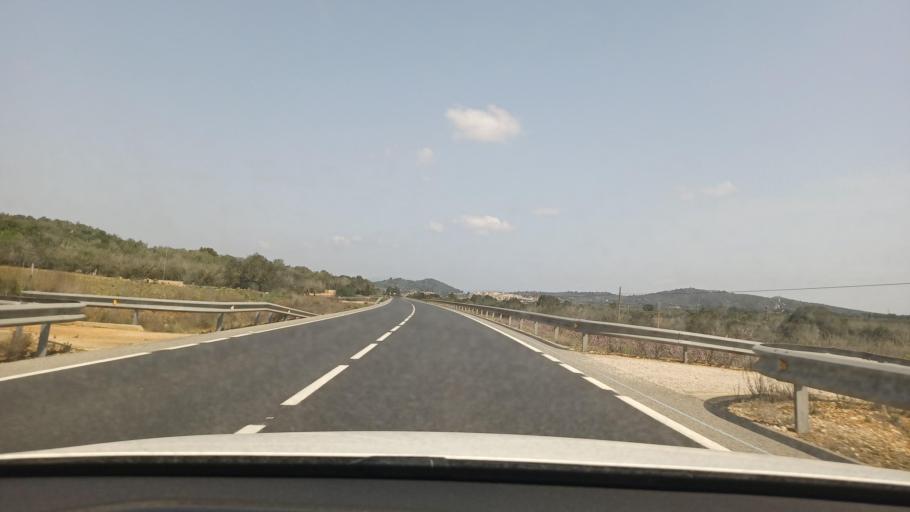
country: ES
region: Catalonia
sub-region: Provincia de Tarragona
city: Santa Barbara
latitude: 40.6508
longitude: 0.5049
